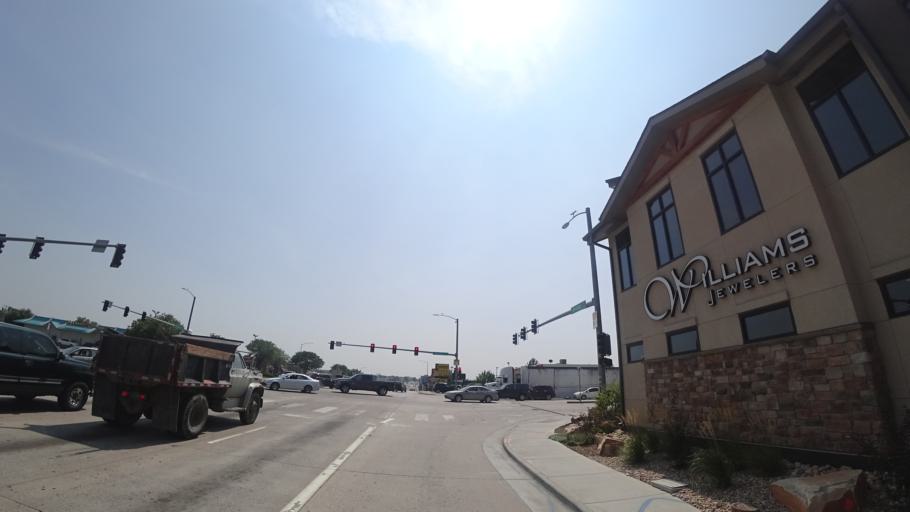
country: US
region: Colorado
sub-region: Arapahoe County
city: Englewood
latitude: 39.6244
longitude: -104.9880
